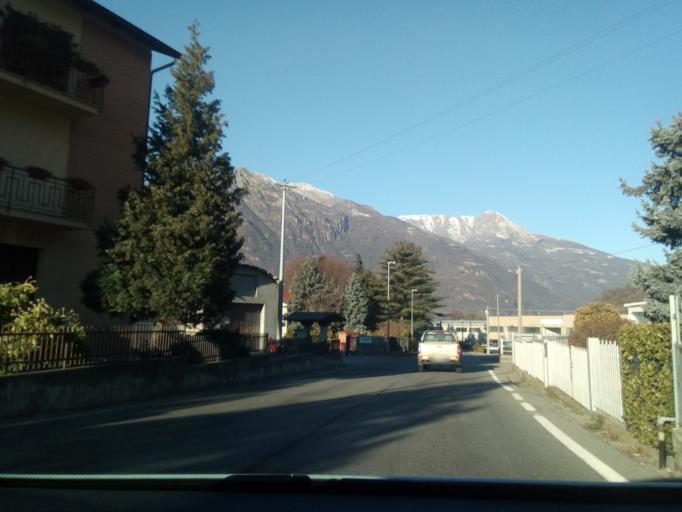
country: IT
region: Piedmont
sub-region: Provincia di Torino
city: Borgofranco d'Ivrea
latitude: 45.5151
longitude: 7.8665
